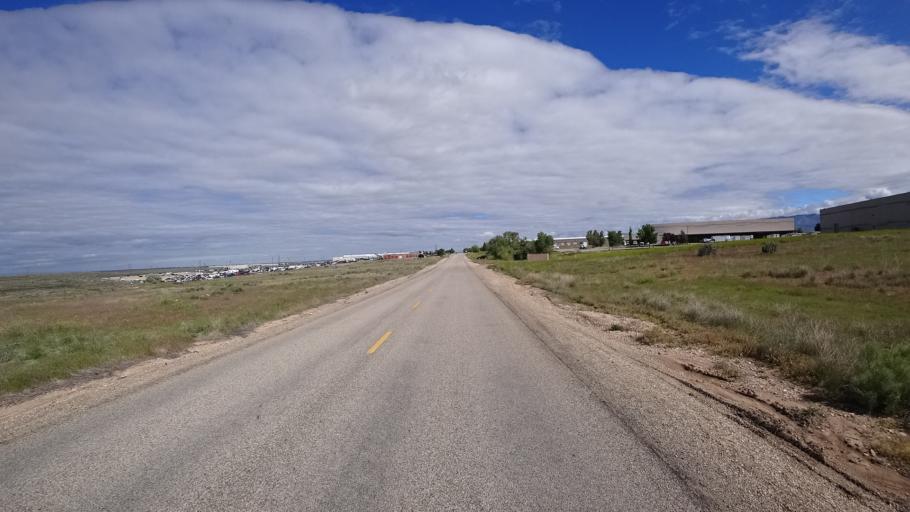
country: US
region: Idaho
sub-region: Ada County
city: Boise
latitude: 43.5307
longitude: -116.1576
